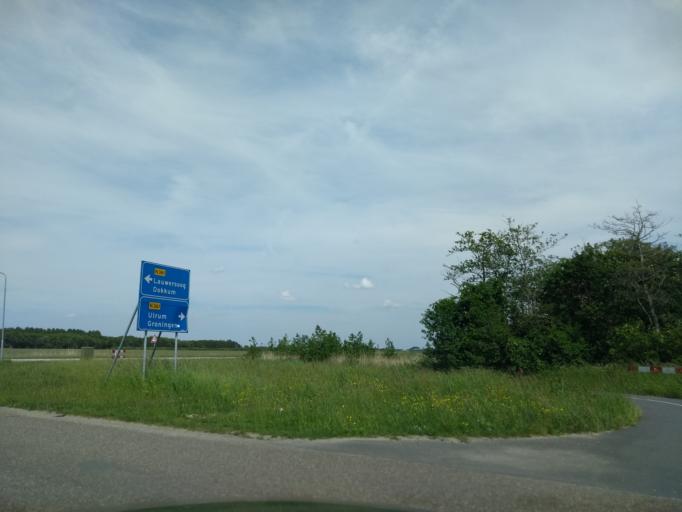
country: NL
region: Groningen
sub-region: Gemeente De Marne
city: Ulrum
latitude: 53.3645
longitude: 6.2605
